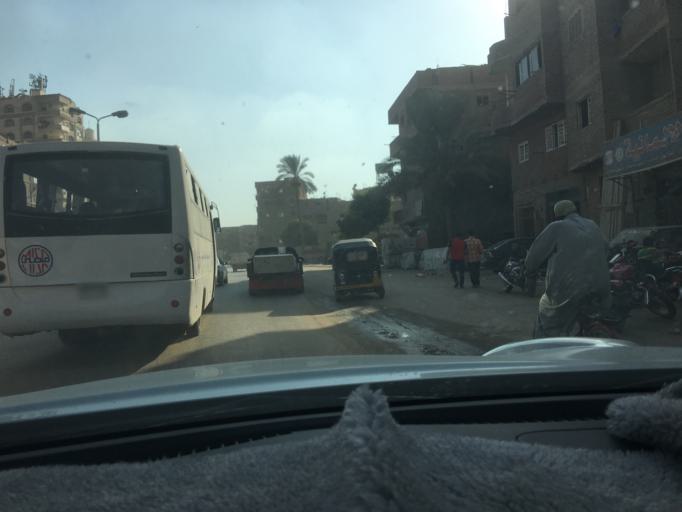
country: EG
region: Muhafazat al Qalyubiyah
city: Al Khankah
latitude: 30.1527
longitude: 31.3726
